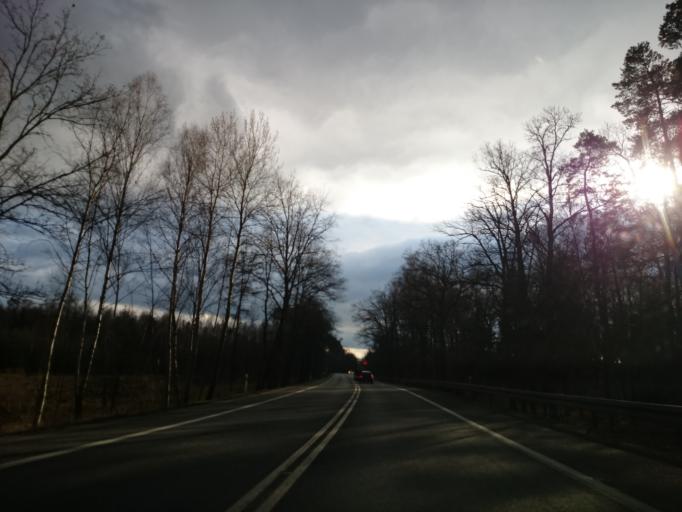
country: PL
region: Opole Voivodeship
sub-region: Powiat opolski
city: Dabrowa
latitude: 50.6729
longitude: 17.7062
